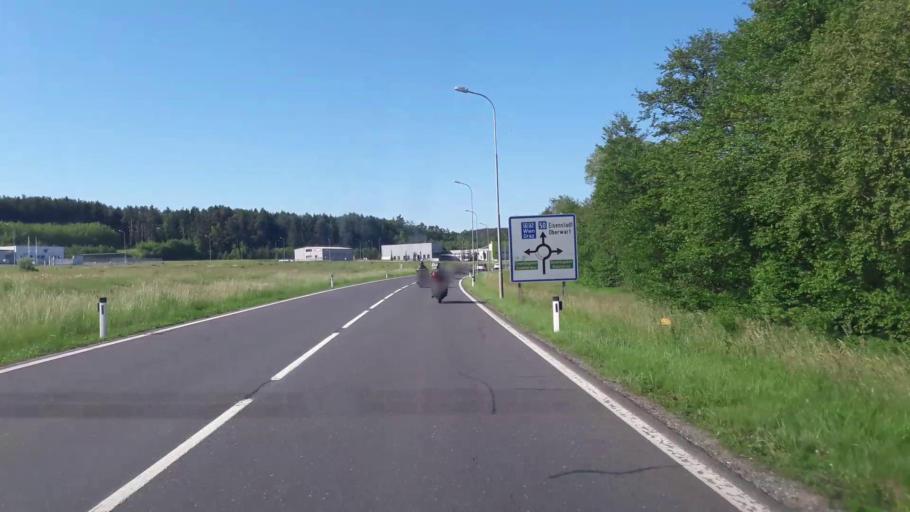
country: AT
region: Burgenland
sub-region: Politischer Bezirk Oberwart
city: Kemeten
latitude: 47.2703
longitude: 16.1527
